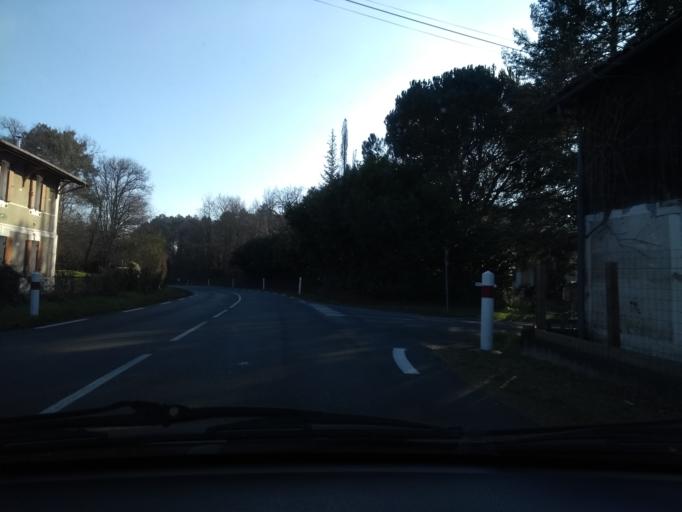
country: FR
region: Aquitaine
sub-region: Departement de la Gironde
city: Salles
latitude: 44.5726
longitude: -0.8830
